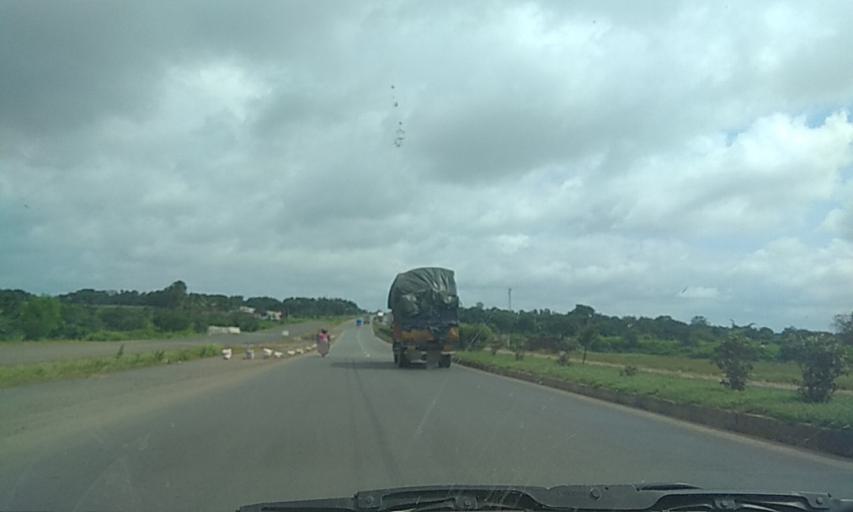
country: IN
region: Karnataka
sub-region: Dharwad
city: Kundgol
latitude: 15.2415
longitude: 75.1431
